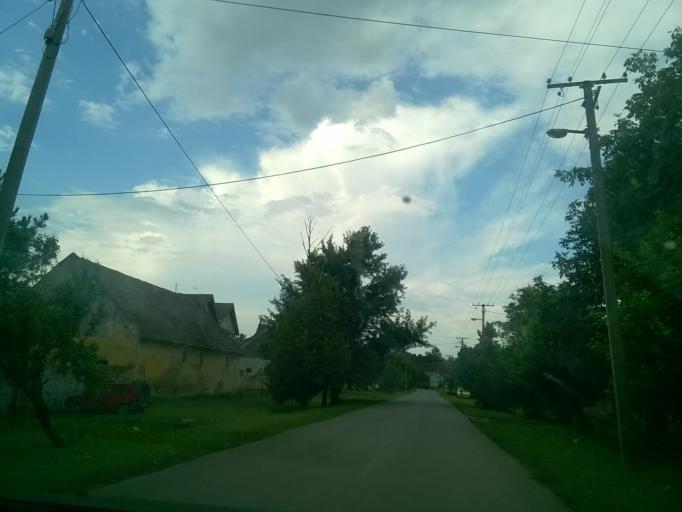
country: RS
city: Tomasevac
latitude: 45.2701
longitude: 20.6223
